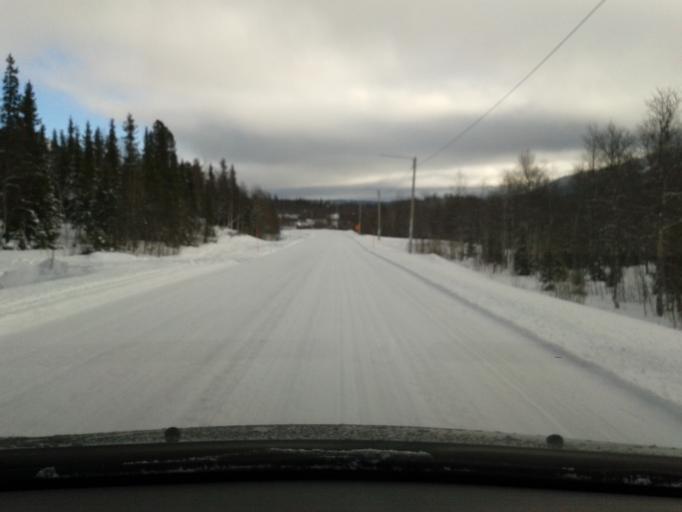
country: SE
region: Vaesterbotten
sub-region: Vilhelmina Kommun
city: Sjoberg
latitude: 65.2522
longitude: 15.5423
